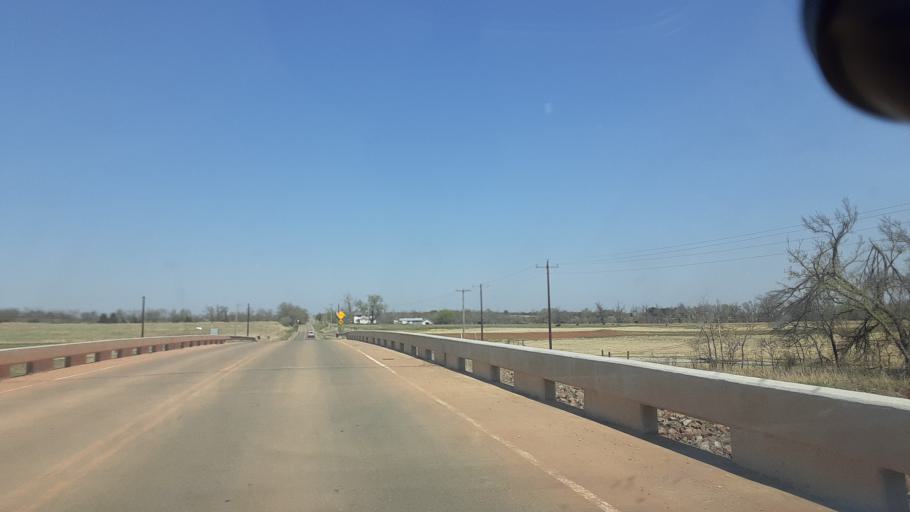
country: US
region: Oklahoma
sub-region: Logan County
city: Guthrie
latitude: 35.8136
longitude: -97.4784
